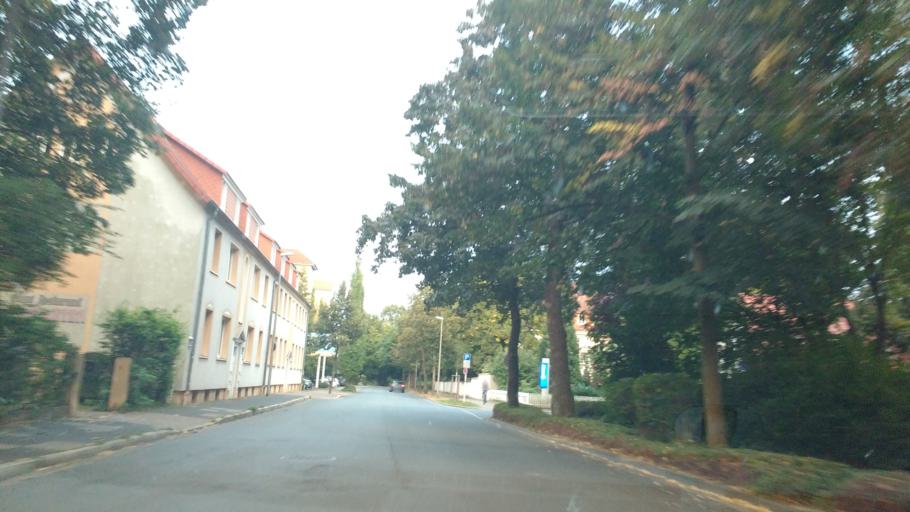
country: DE
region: North Rhine-Westphalia
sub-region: Regierungsbezirk Detmold
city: Minden
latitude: 52.2846
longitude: 8.9130
